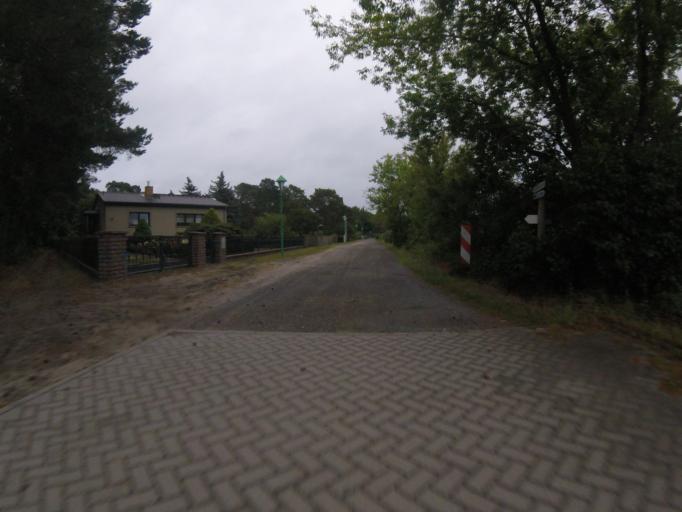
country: DE
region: Brandenburg
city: Bestensee
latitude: 52.2359
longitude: 13.7189
